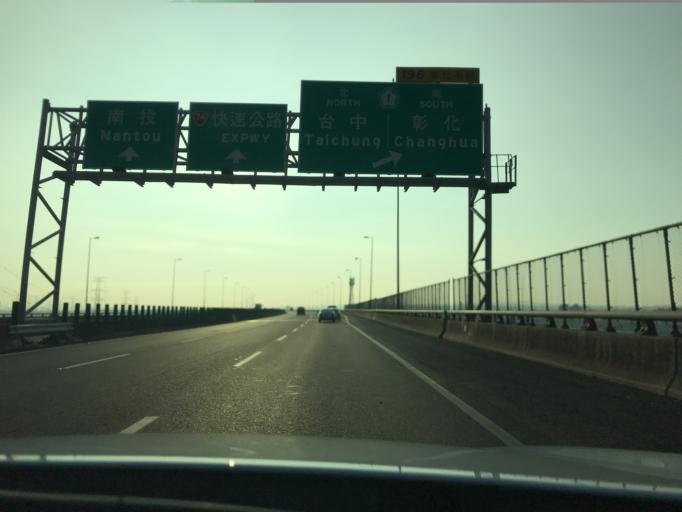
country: TW
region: Taiwan
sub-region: Changhua
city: Chang-hua
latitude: 24.1121
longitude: 120.5442
